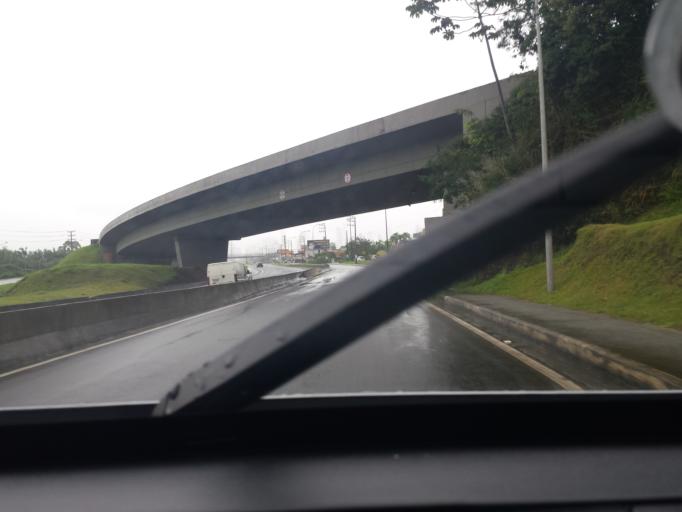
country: BR
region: Santa Catarina
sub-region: Balneario Camboriu
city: Balneario Camboriu
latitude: -27.0288
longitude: -48.6051
